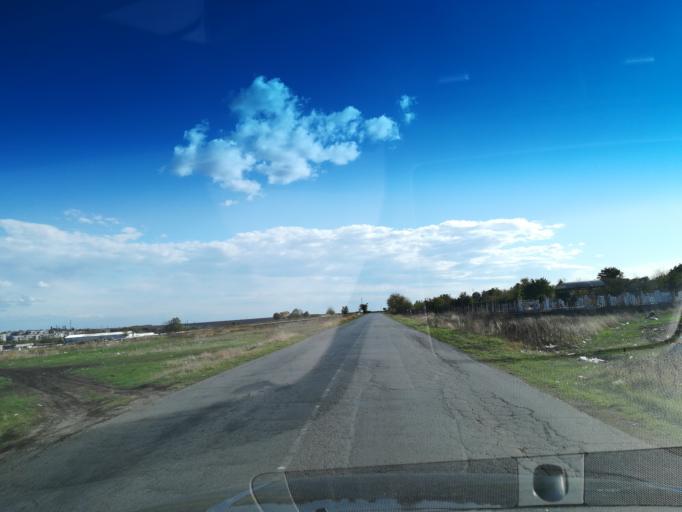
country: BG
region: Stara Zagora
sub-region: Obshtina Chirpan
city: Chirpan
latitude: 42.1999
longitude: 25.3103
